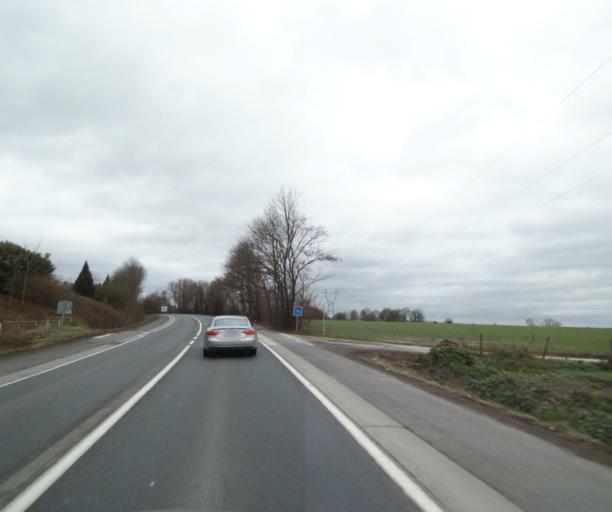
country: FR
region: Nord-Pas-de-Calais
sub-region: Departement du Nord
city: Saint-Saulve
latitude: 50.3721
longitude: 3.5701
